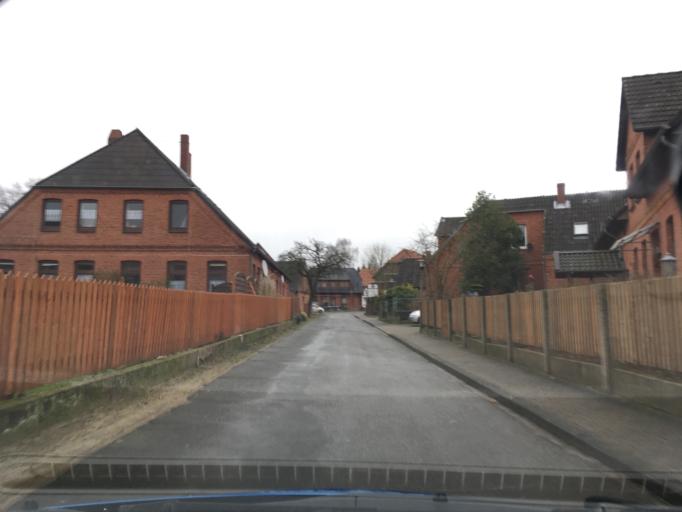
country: DE
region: Lower Saxony
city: Neetze
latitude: 53.2665
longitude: 10.6252
